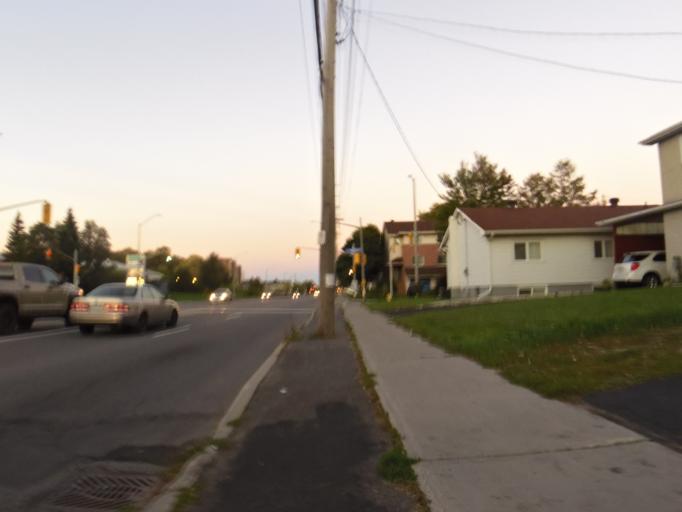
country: CA
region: Ontario
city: Ottawa
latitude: 45.3719
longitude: -75.6593
